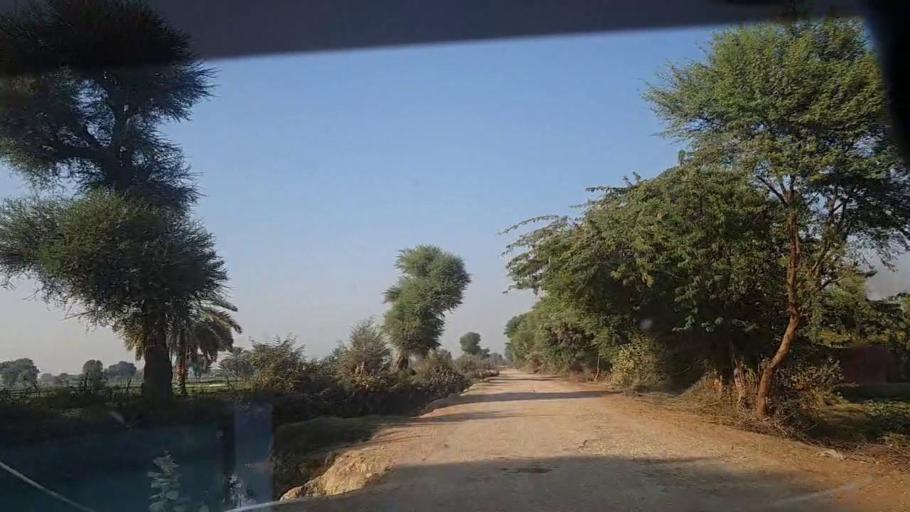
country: PK
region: Sindh
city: Sobhadero
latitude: 27.2597
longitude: 68.3508
